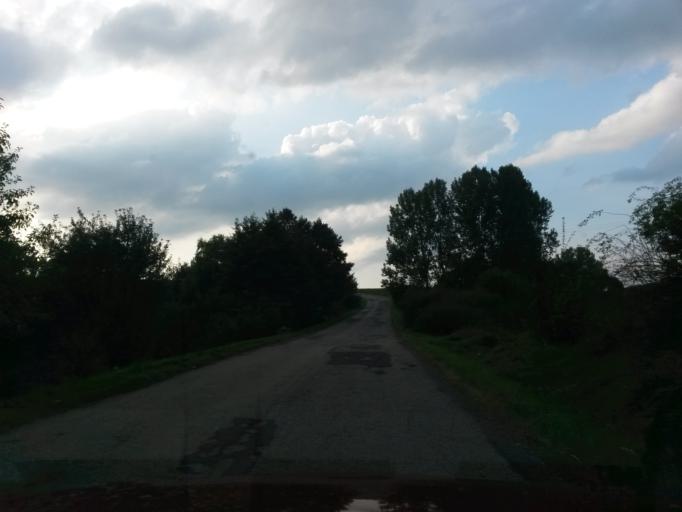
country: SK
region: Kosicky
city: Secovce
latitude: 48.8022
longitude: 21.4740
